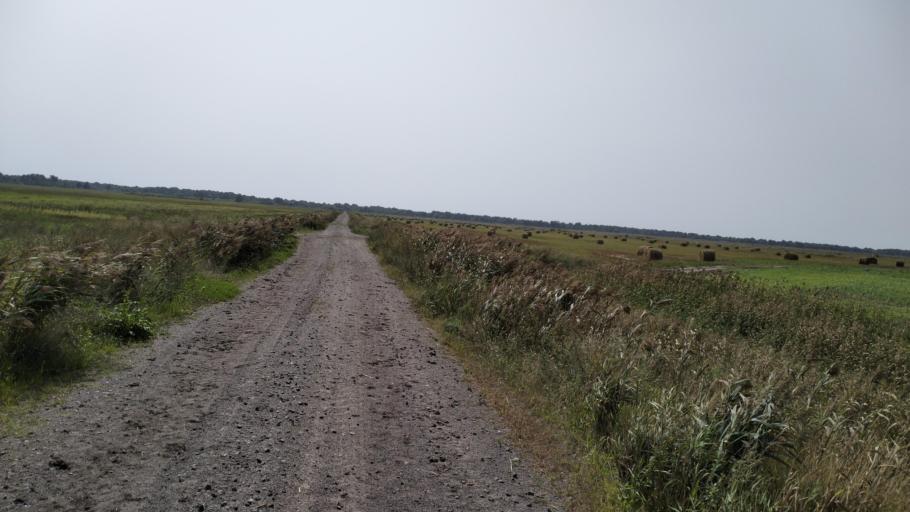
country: BY
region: Brest
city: Davyd-Haradok
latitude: 51.9821
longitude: 27.1750
